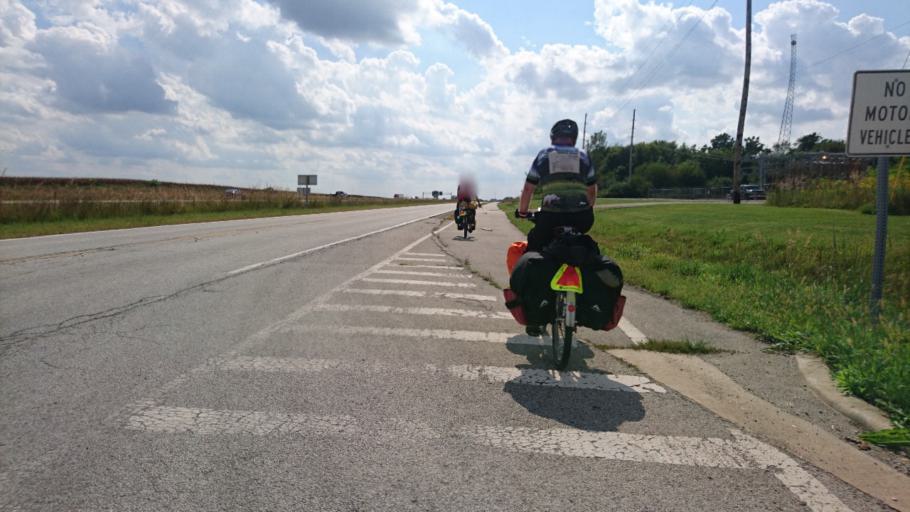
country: US
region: Illinois
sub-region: McLean County
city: Bloomington
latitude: 40.4293
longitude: -89.0359
